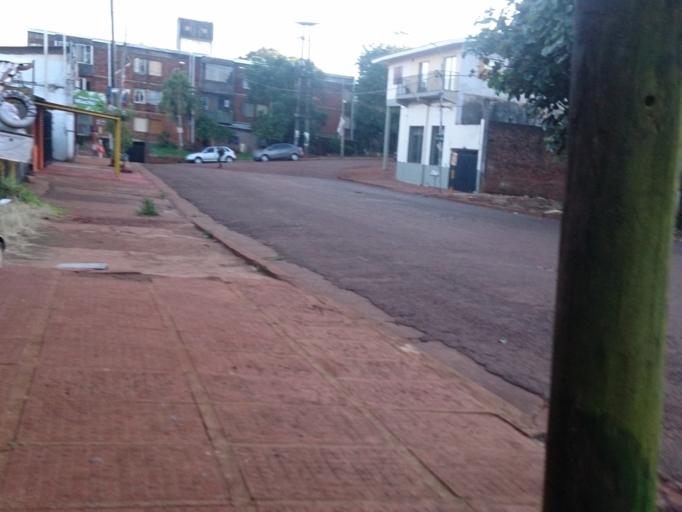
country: AR
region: Misiones
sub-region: Departamento de Obera
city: Obera
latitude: -27.4915
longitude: -55.1030
